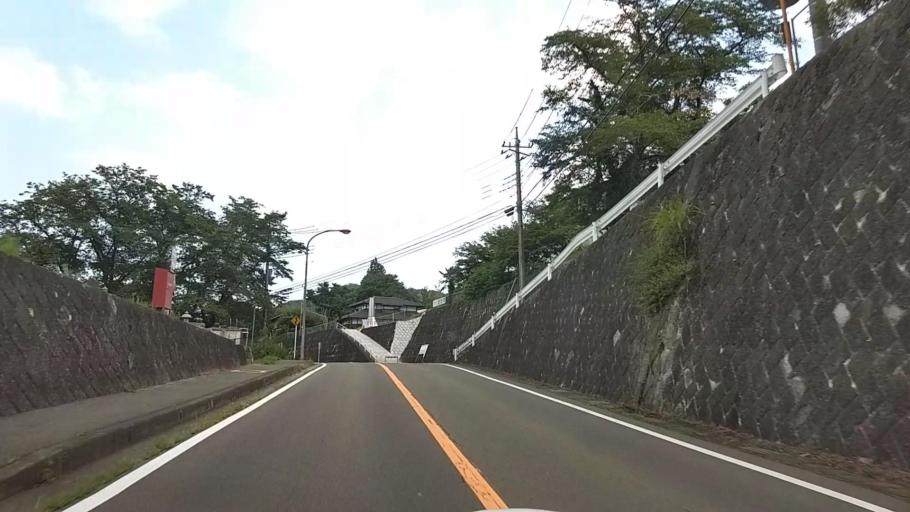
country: JP
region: Yamanashi
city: Uenohara
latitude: 35.6118
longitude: 139.1484
